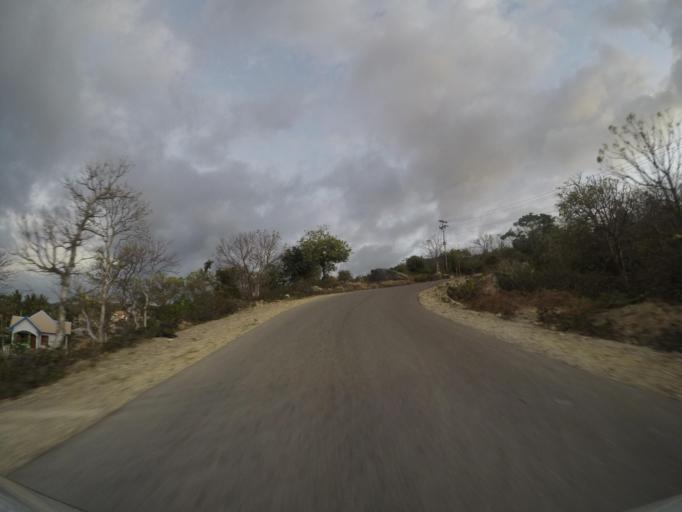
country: TL
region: Lautem
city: Lospalos
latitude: -8.3591
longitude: 127.0569
